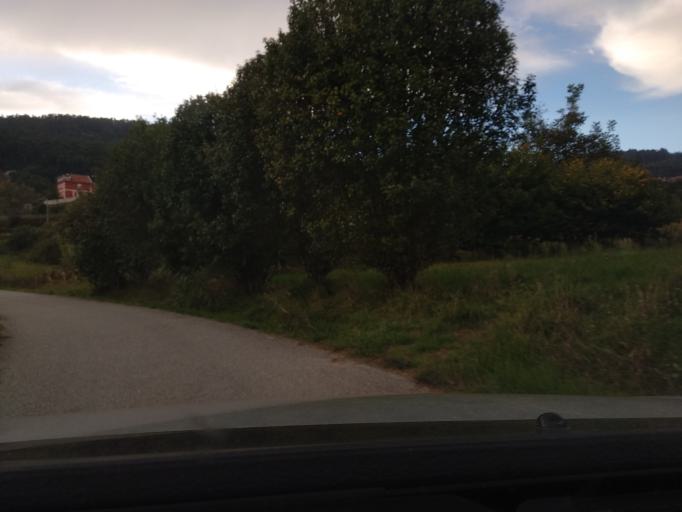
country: ES
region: Galicia
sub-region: Provincia de Pontevedra
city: Moana
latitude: 42.2983
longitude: -8.7352
